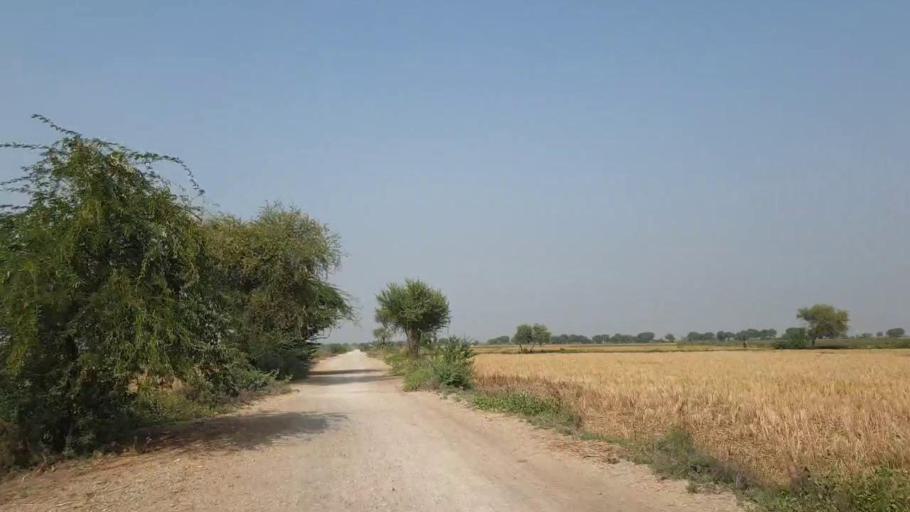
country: PK
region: Sindh
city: Kario
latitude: 24.9398
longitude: 68.5573
